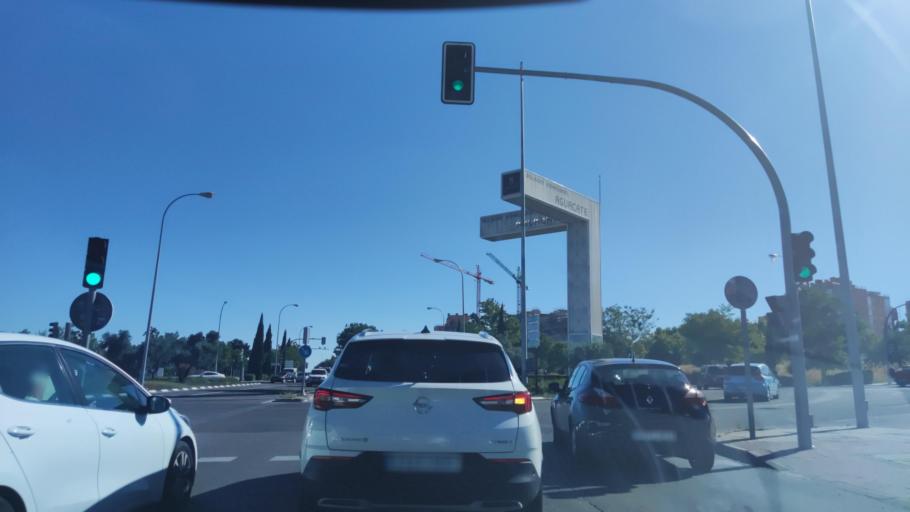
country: ES
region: Madrid
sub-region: Provincia de Madrid
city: Latina
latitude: 40.3680
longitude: -3.7408
